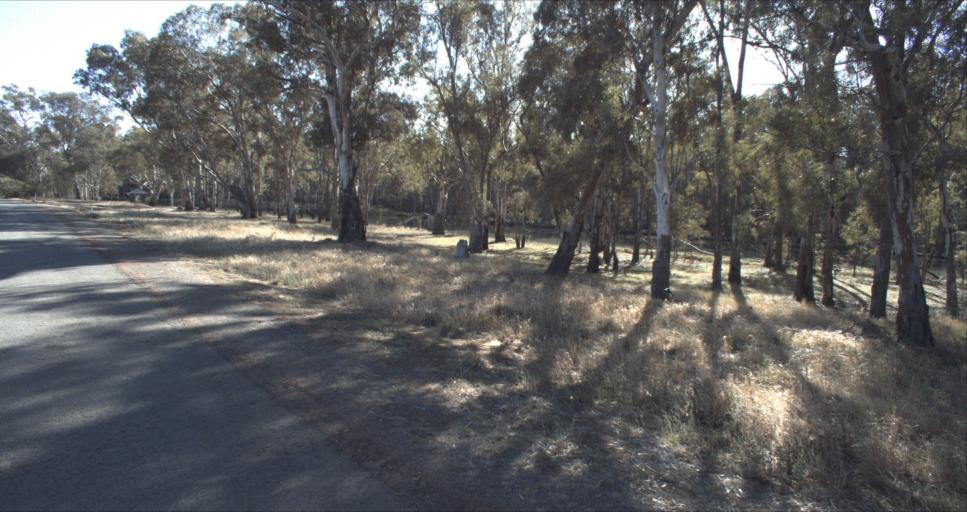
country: AU
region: New South Wales
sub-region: Leeton
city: Leeton
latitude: -34.6130
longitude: 146.2596
